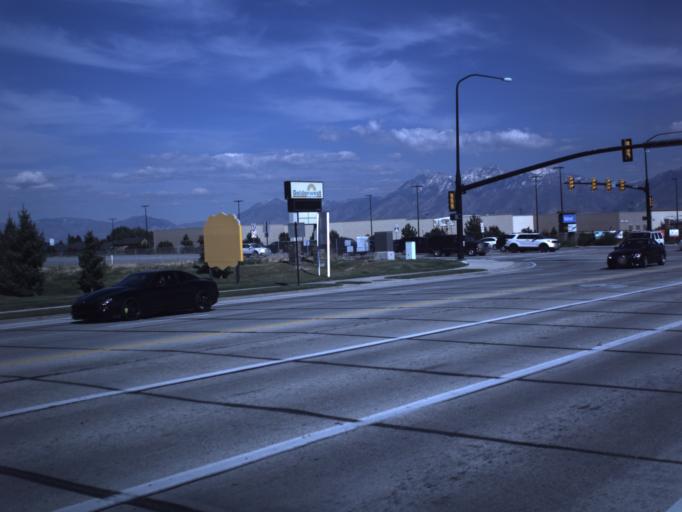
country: US
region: Utah
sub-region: Salt Lake County
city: South Jordan Heights
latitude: 40.5618
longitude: -111.9780
